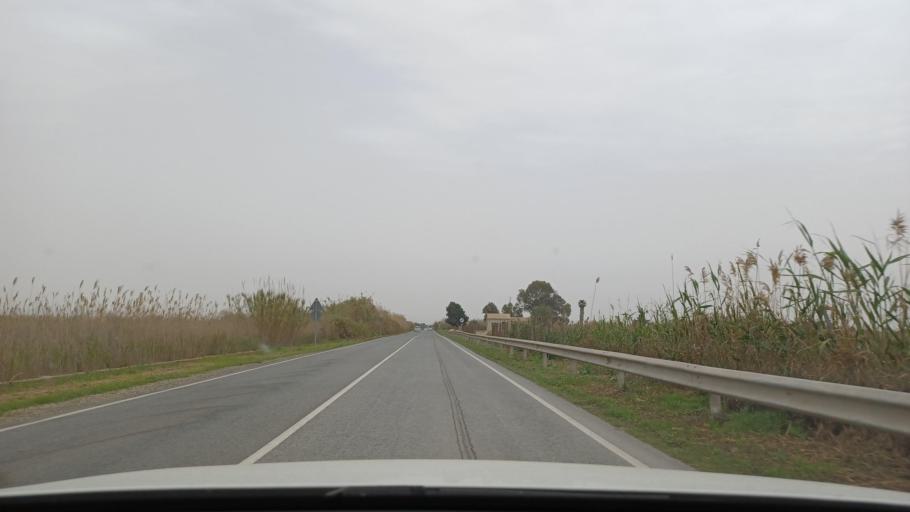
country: ES
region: Valencia
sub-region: Provincia de Alicante
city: Daya Vieja
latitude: 38.1663
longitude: -0.7026
